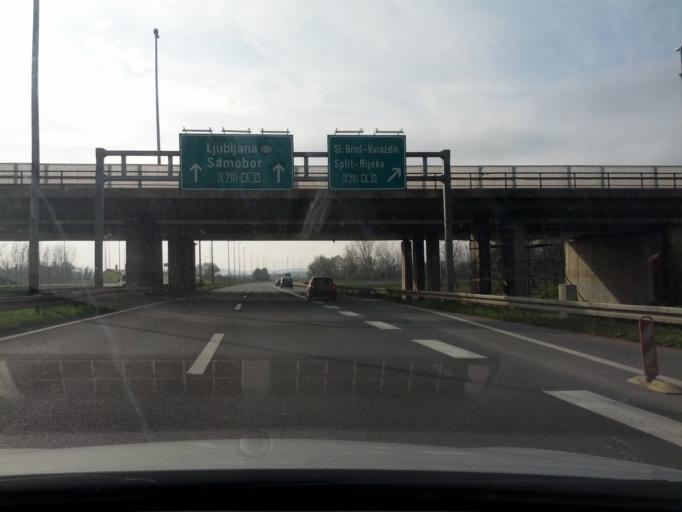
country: HR
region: Grad Zagreb
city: Jezdovec
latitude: 45.7897
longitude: 15.8498
